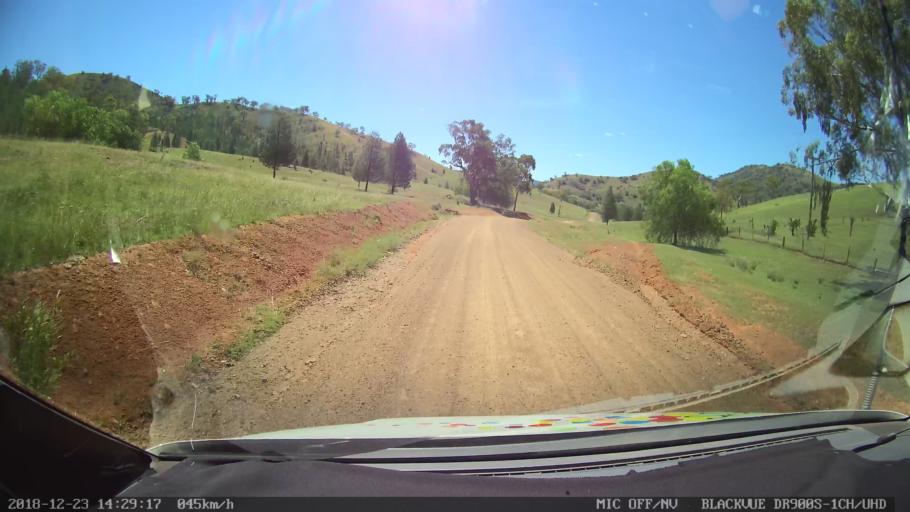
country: AU
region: New South Wales
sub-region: Tamworth Municipality
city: Manilla
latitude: -30.6095
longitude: 150.9384
